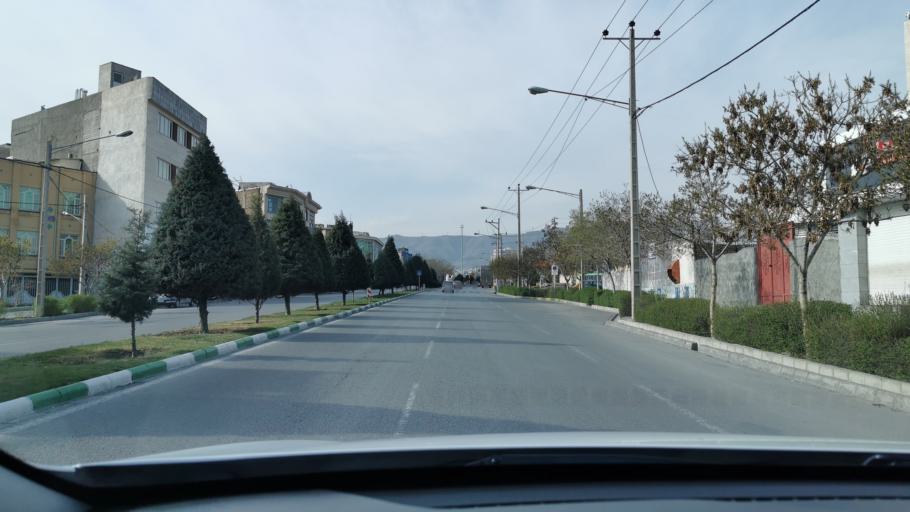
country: IR
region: Razavi Khorasan
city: Mashhad
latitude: 36.3068
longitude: 59.5138
